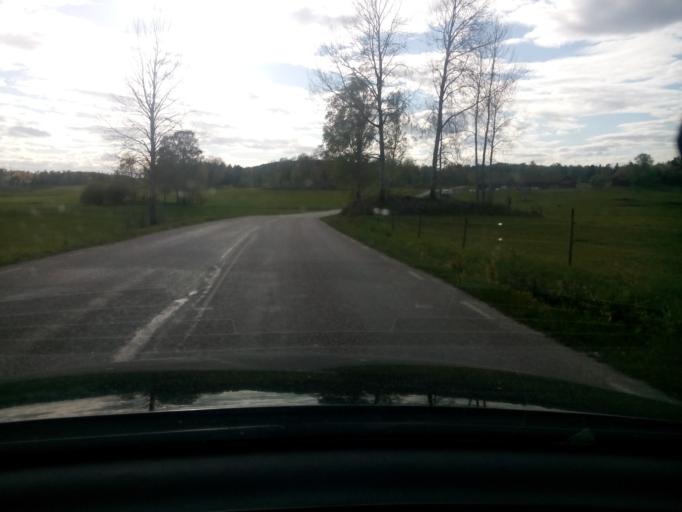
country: SE
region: Soedermanland
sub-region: Nykopings Kommun
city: Stigtomta
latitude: 58.9517
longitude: 16.8692
